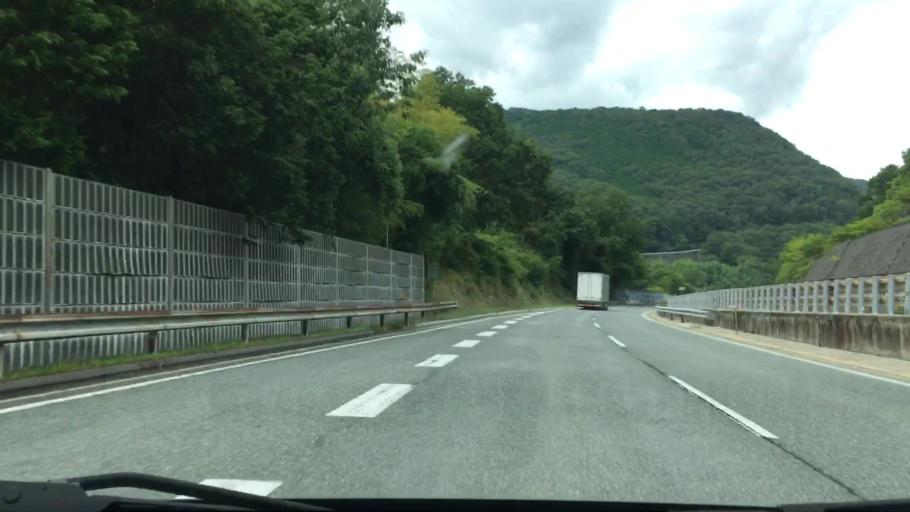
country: JP
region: Okayama
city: Niimi
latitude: 34.9659
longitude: 133.6307
